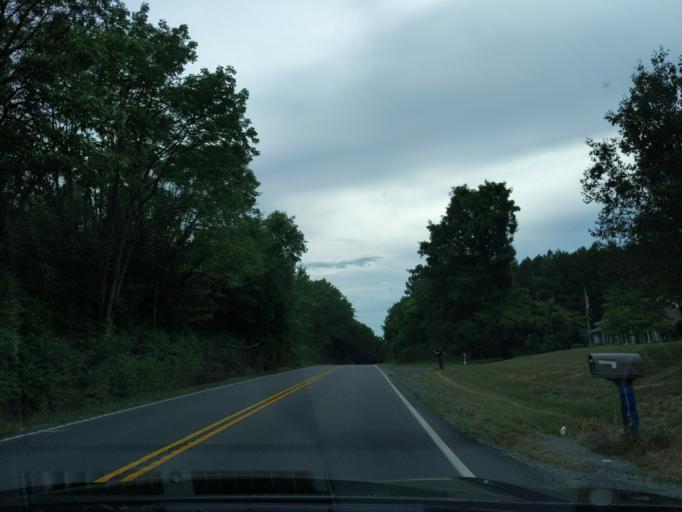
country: US
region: North Carolina
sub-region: Cabarrus County
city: Mount Pleasant
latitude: 35.4377
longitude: -80.3798
